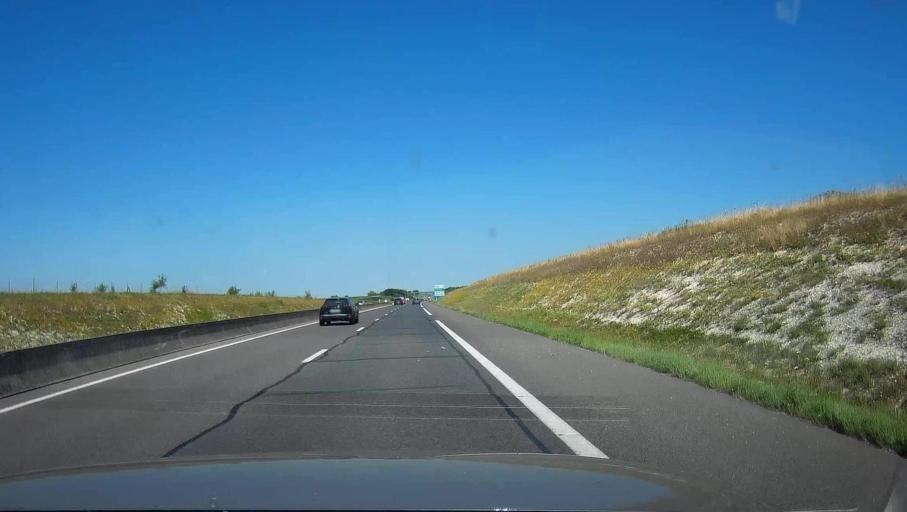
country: FR
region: Champagne-Ardenne
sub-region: Departement de la Marne
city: Fagnieres
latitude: 48.9143
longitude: 4.2833
